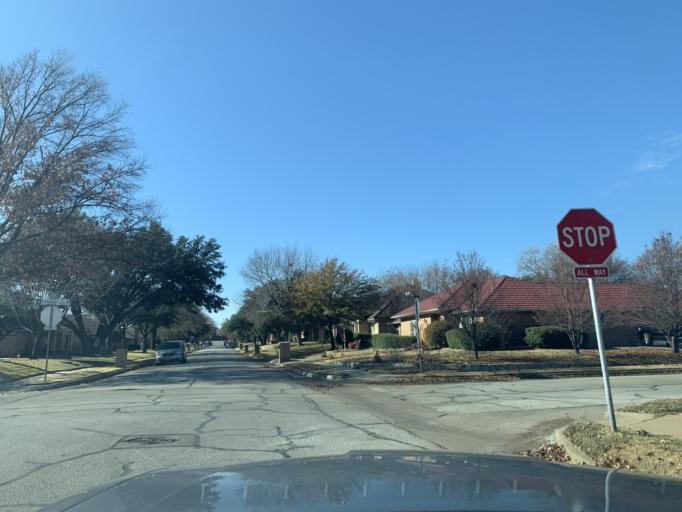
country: US
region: Texas
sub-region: Tarrant County
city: Bedford
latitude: 32.8442
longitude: -97.1534
